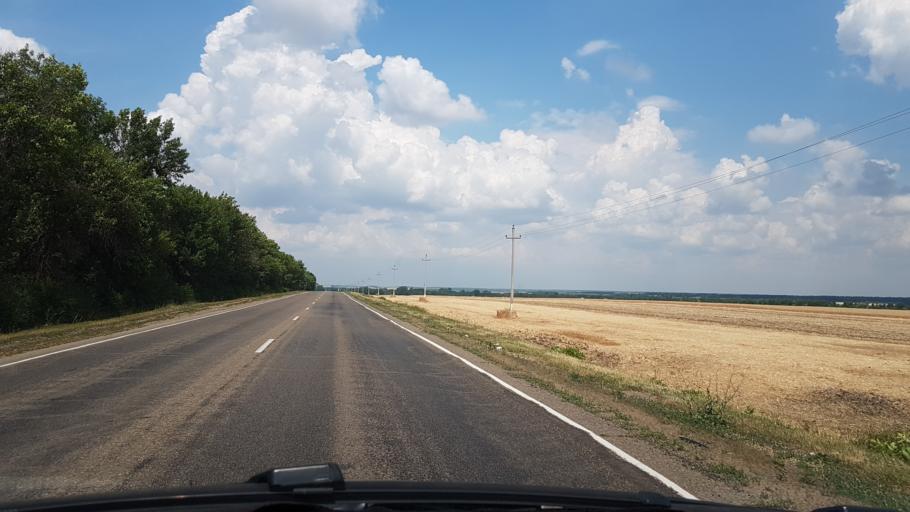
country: RU
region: Krasnodarskiy
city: Dmitriyevskaya
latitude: 45.6914
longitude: 40.7442
